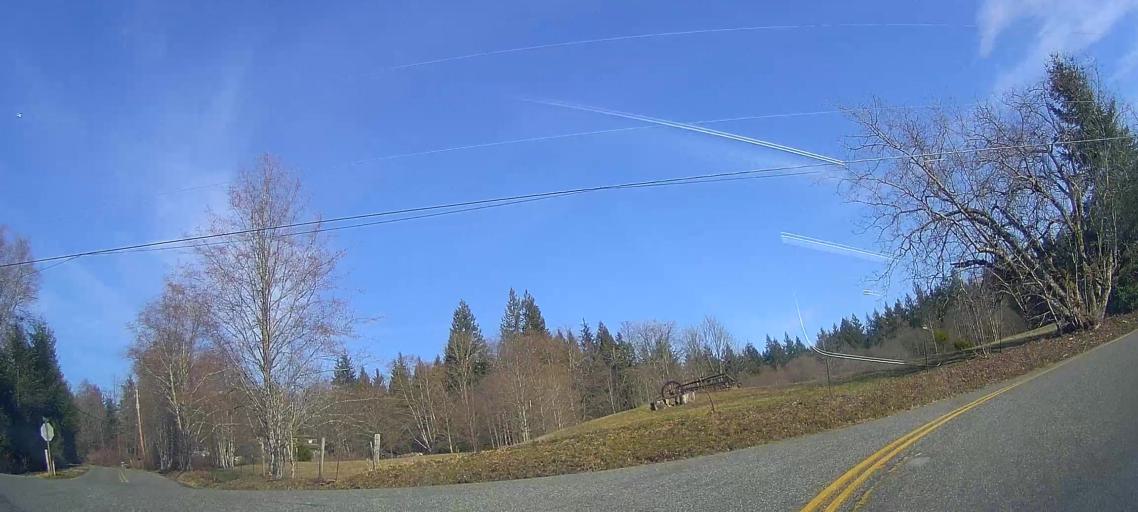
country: US
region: Washington
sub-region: Whatcom County
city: Sudden Valley
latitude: 48.5976
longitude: -122.3673
